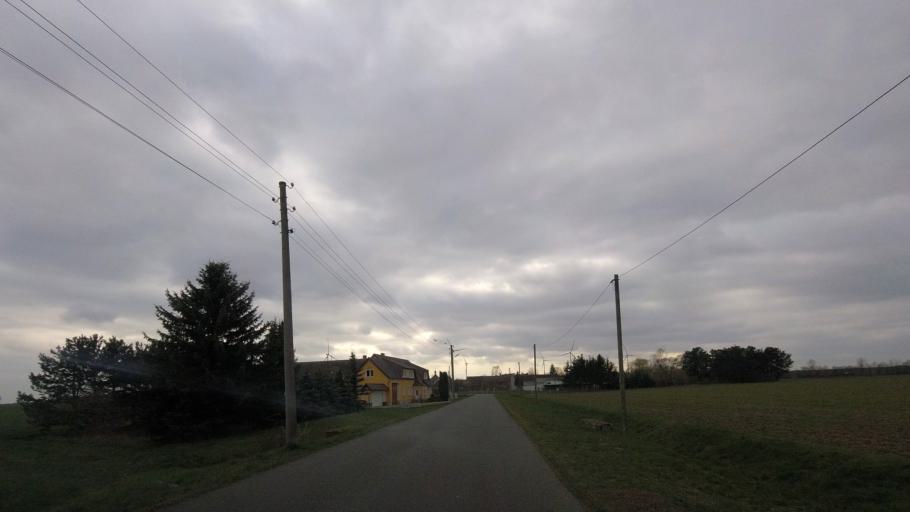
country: DE
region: Saxony-Anhalt
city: Seyda
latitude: 51.9261
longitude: 12.8943
